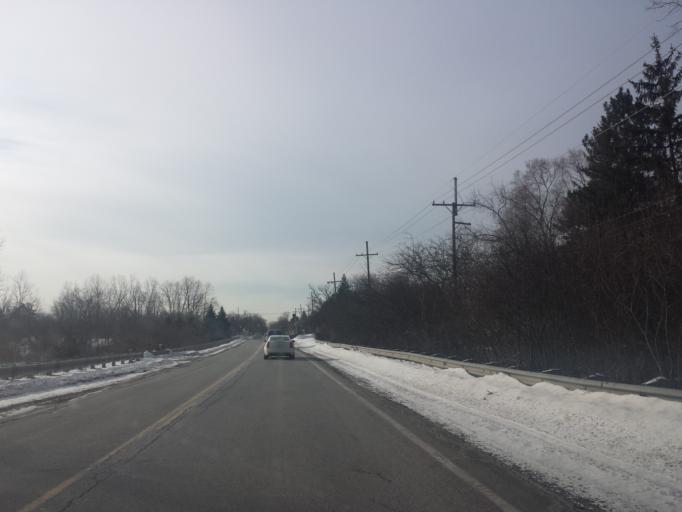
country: US
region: Michigan
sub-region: Oakland County
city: Orchard Lake
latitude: 42.5465
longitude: -83.3413
